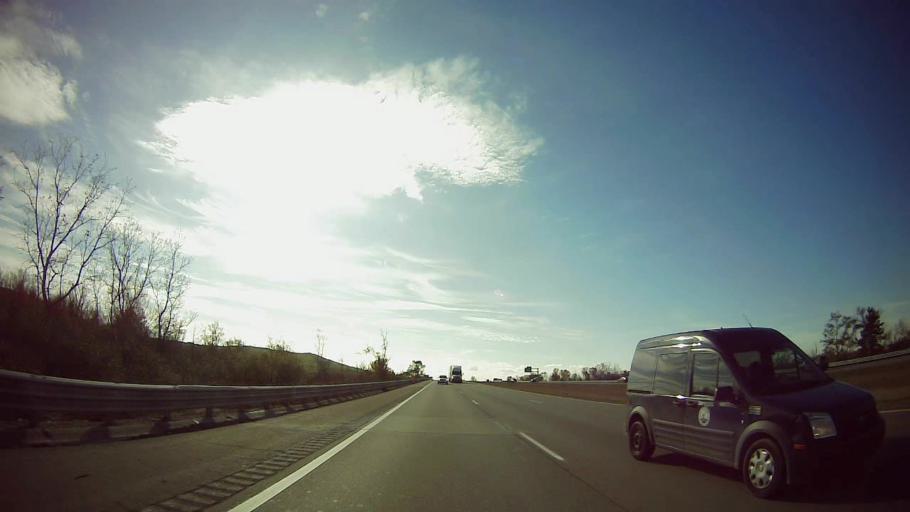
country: US
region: Michigan
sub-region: Wayne County
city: Wayne
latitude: 42.2712
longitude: -83.4408
